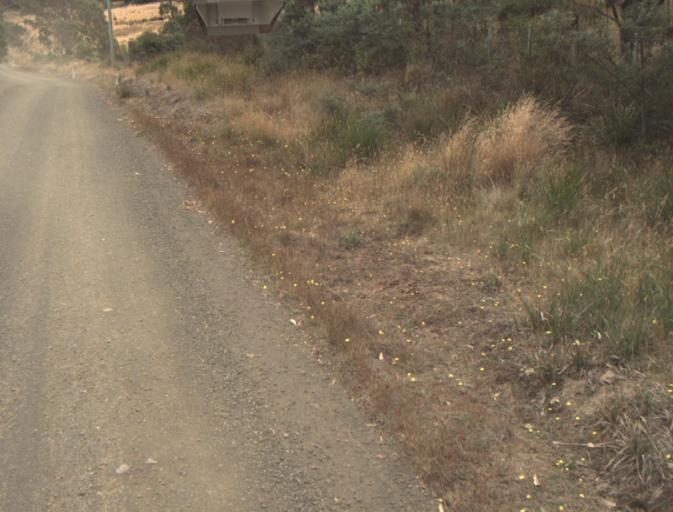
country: AU
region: Tasmania
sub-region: Northern Midlands
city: Evandale
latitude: -41.5242
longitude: 147.4581
